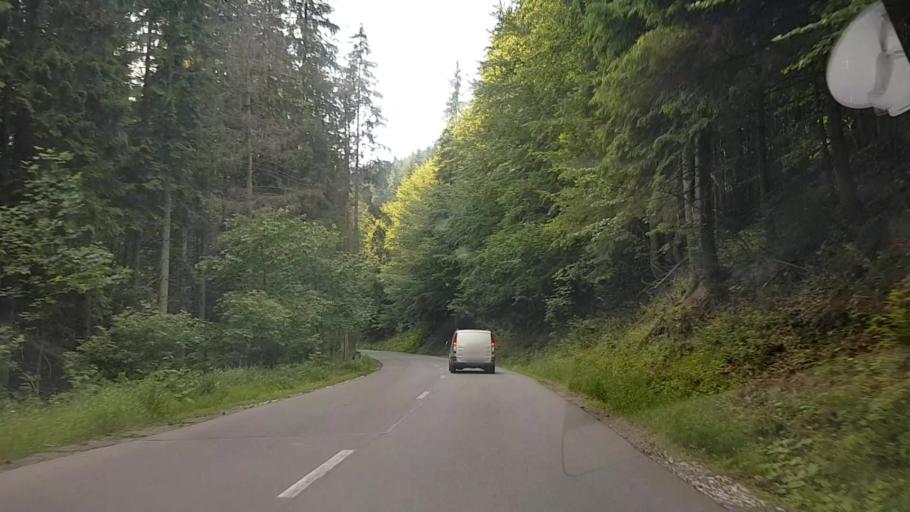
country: RO
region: Harghita
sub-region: Comuna Varsag
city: Varsag
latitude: 46.6715
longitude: 25.3286
